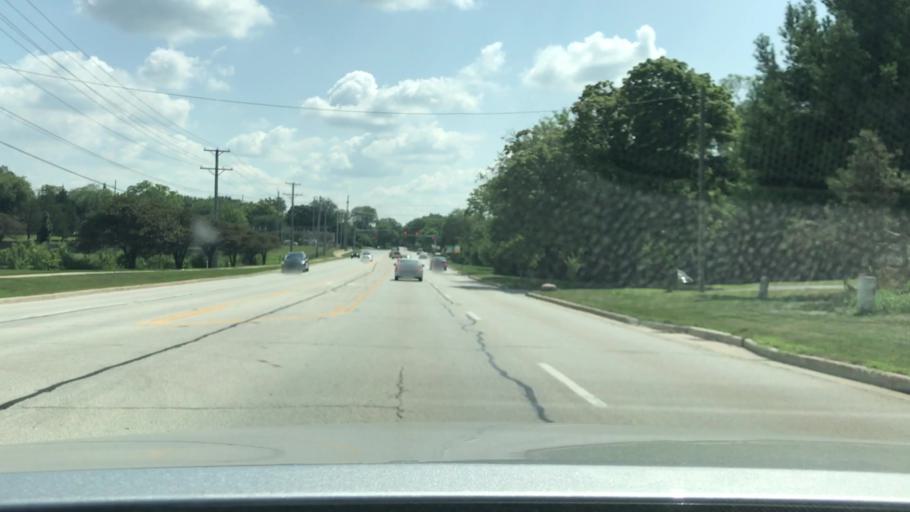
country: US
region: Illinois
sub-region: DuPage County
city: Woodridge
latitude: 41.7292
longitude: -88.0154
